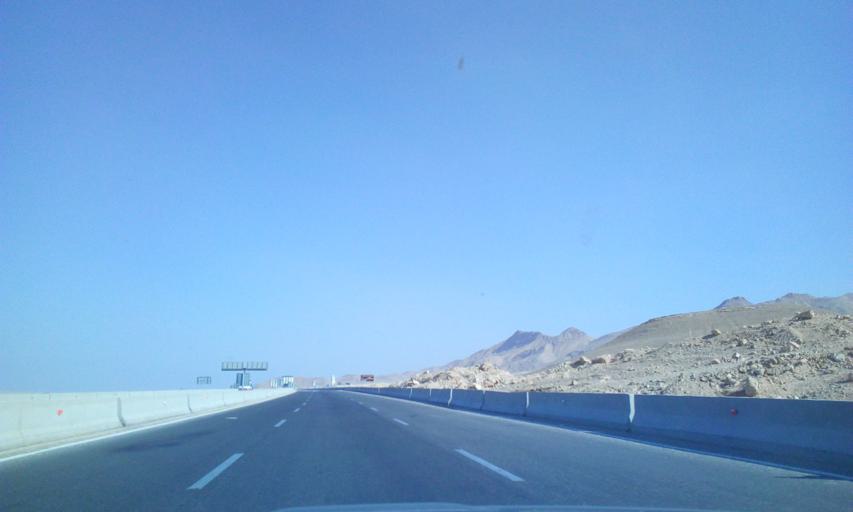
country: EG
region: As Suways
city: Ain Sukhna
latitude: 29.4514
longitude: 32.3390
